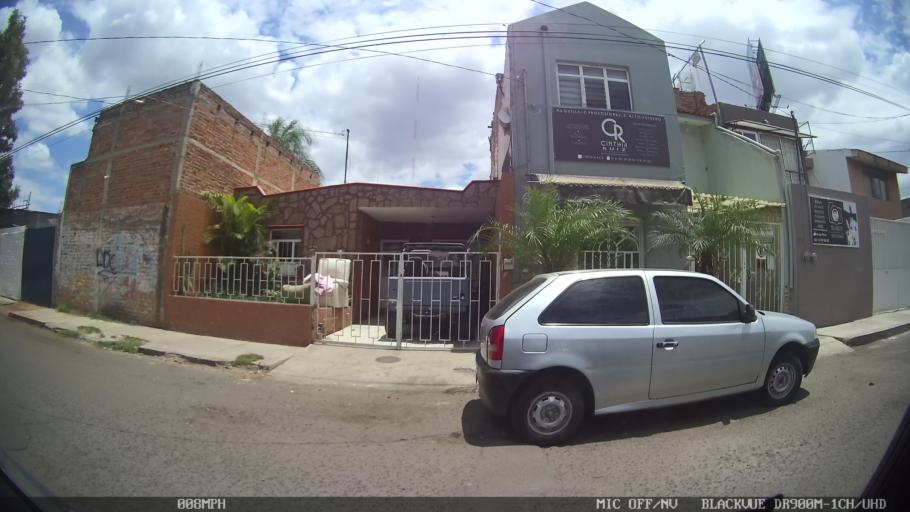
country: MX
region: Jalisco
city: Tlaquepaque
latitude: 20.6344
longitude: -103.2708
